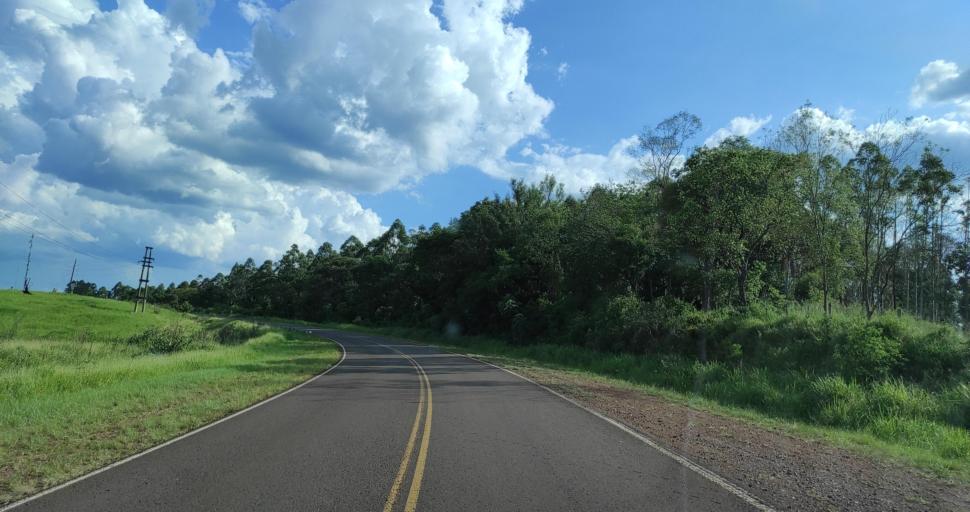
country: AR
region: Misiones
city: San Vicente
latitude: -26.3600
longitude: -54.2159
